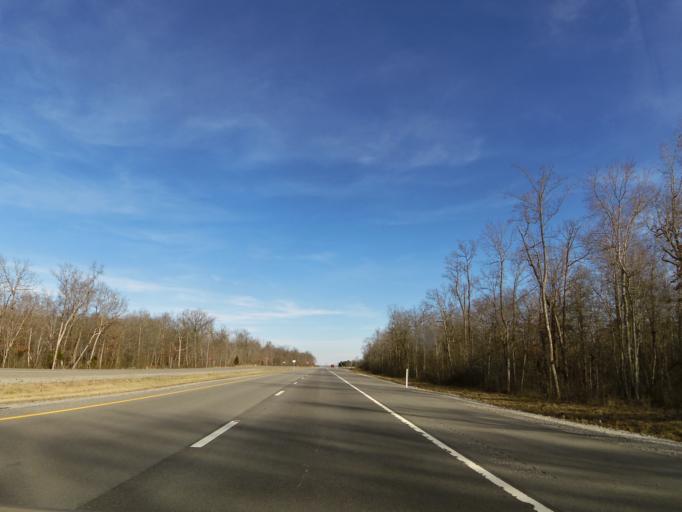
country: US
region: Tennessee
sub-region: Warren County
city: McMinnville
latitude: 35.7174
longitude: -85.8650
